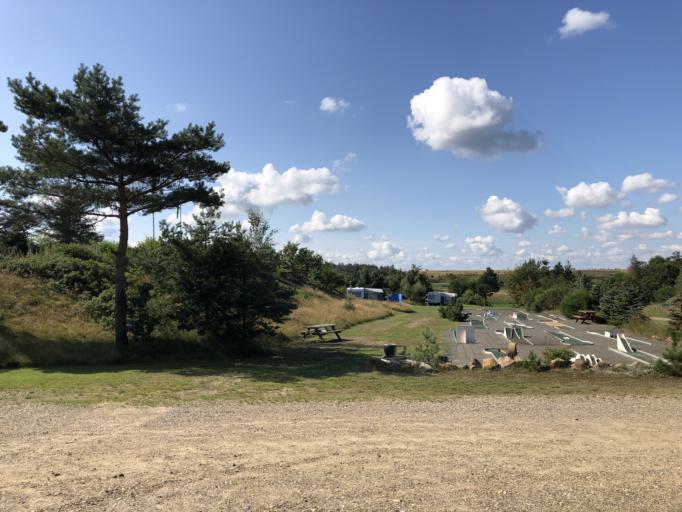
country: DK
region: Central Jutland
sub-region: Skive Kommune
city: Skive
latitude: 56.5227
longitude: 8.9598
